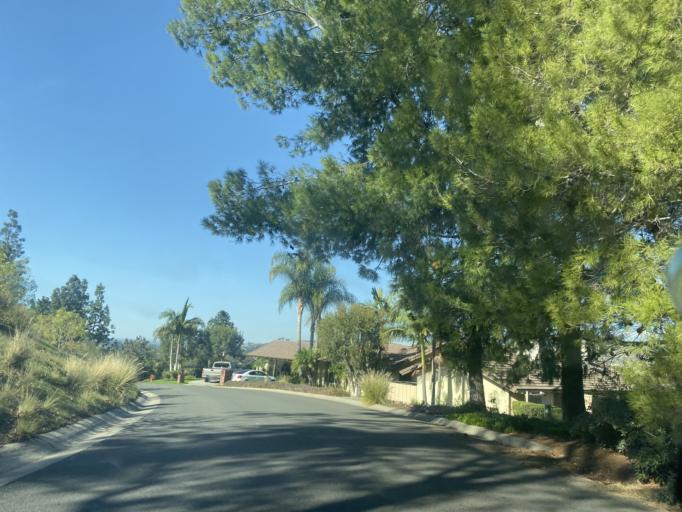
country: US
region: California
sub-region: Orange County
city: Villa Park
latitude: 33.8095
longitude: -117.7729
